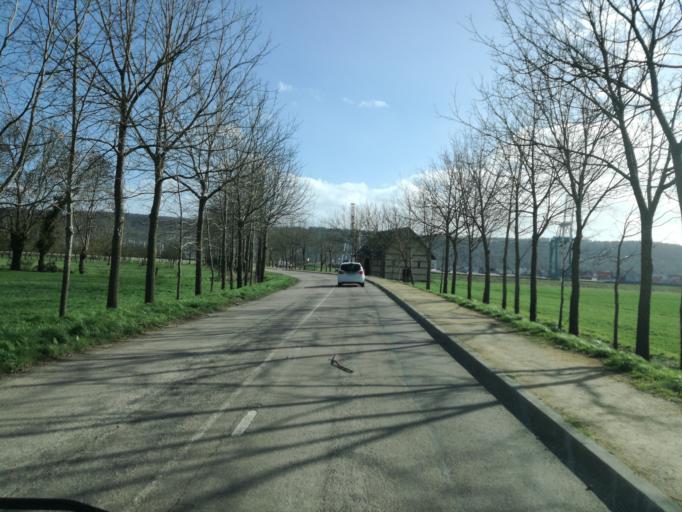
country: FR
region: Haute-Normandie
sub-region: Departement de la Seine-Maritime
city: Grand-Couronne
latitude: 49.3589
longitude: 0.9802
